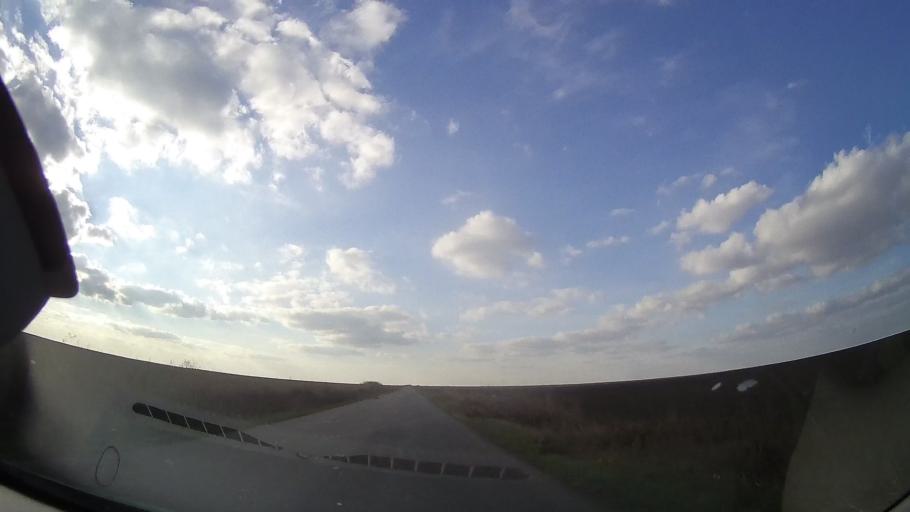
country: RO
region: Constanta
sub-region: Comuna Negru Voda
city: Negru Voda
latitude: 43.8228
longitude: 28.1521
